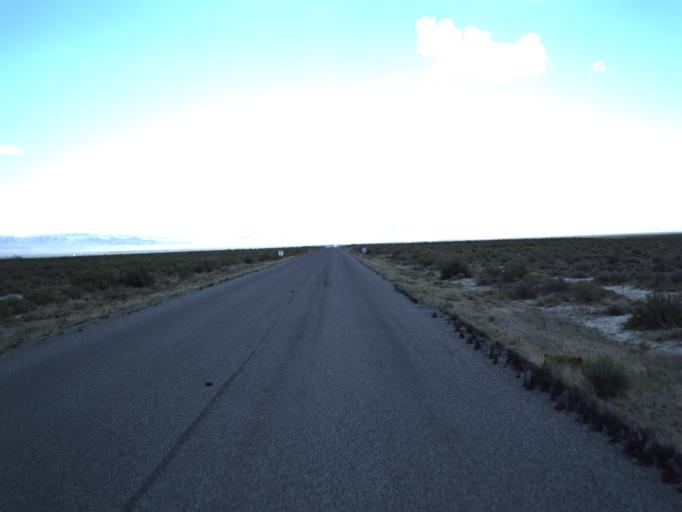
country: US
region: Nevada
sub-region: White Pine County
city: McGill
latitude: 39.0557
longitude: -114.0303
